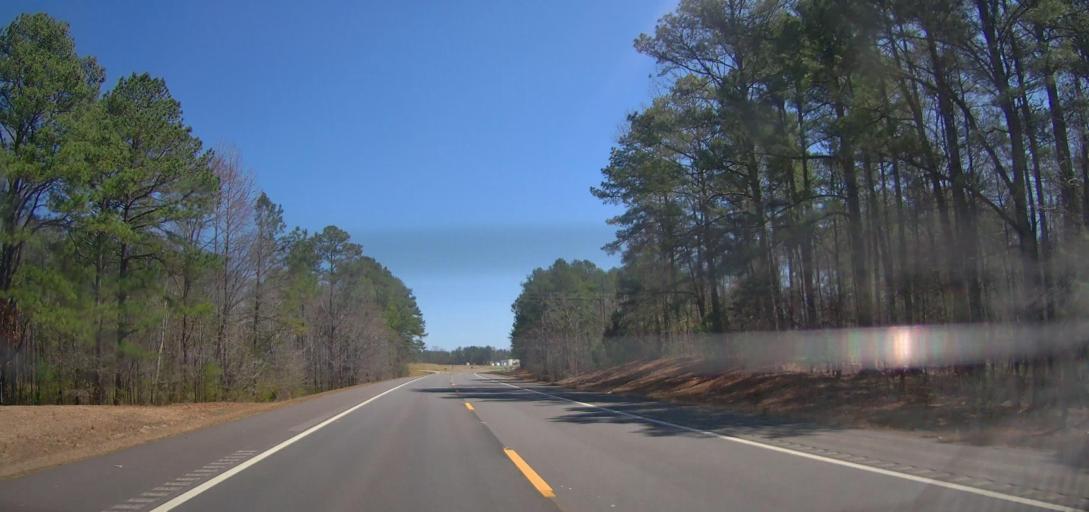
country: US
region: Alabama
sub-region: Calhoun County
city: Ohatchee
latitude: 33.7843
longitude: -86.0196
